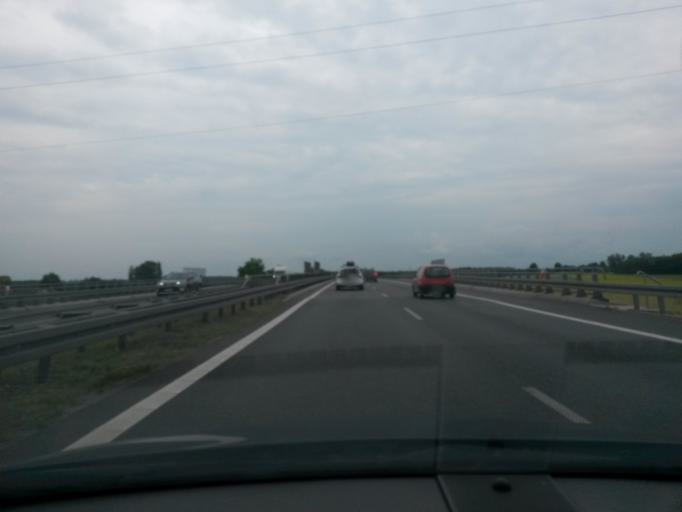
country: PL
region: Masovian Voivodeship
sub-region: Powiat zyrardowski
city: Mszczonow
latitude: 51.9681
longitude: 20.5016
